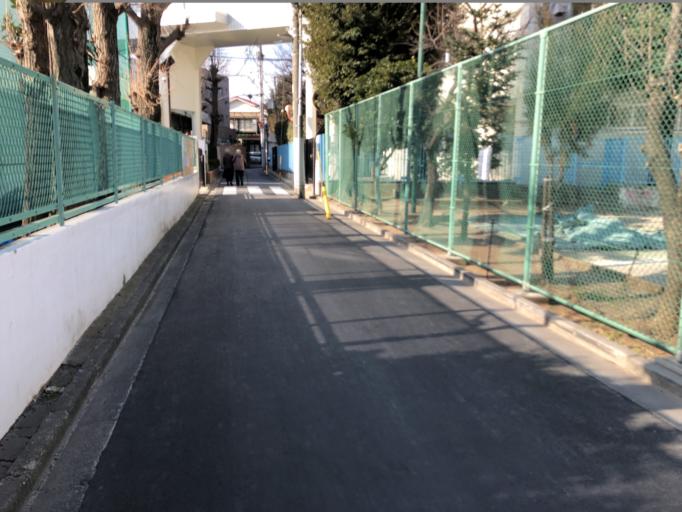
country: JP
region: Tokyo
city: Tokyo
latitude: 35.7285
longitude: 139.7589
